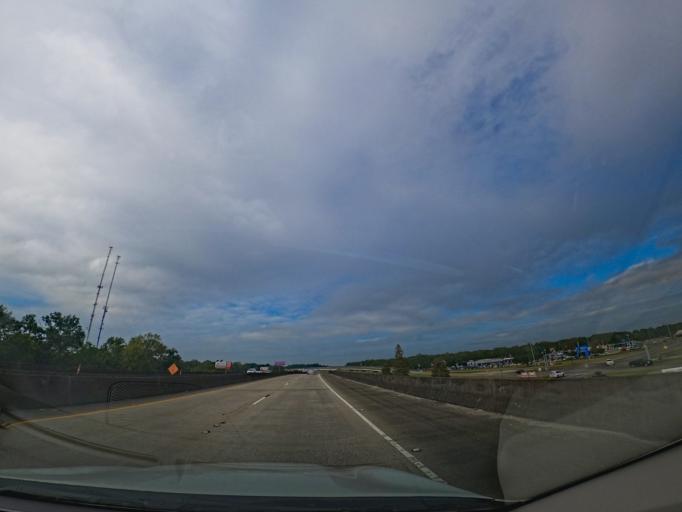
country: US
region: Louisiana
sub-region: Saint Mary Parish
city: Berwick
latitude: 29.6924
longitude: -91.2224
